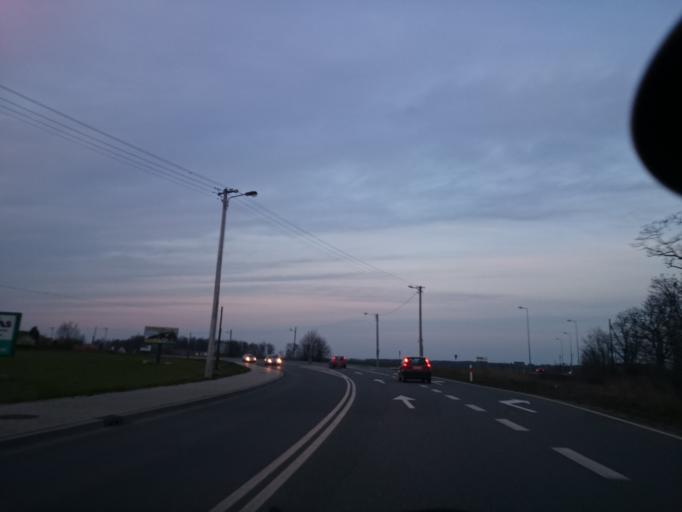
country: PL
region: Opole Voivodeship
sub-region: Powiat prudnicki
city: Biala
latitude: 50.4292
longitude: 17.7440
